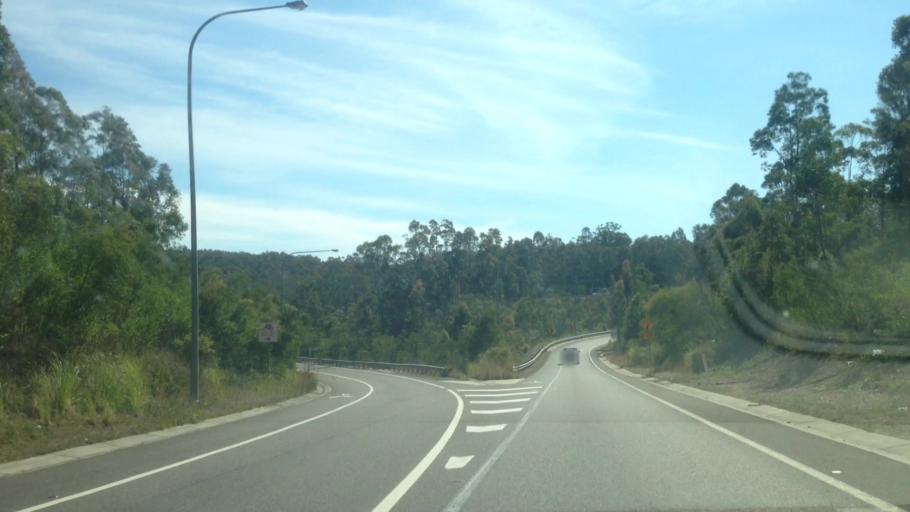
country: AU
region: New South Wales
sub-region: Lake Macquarie Shire
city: Holmesville
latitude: -32.8901
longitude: 151.5972
